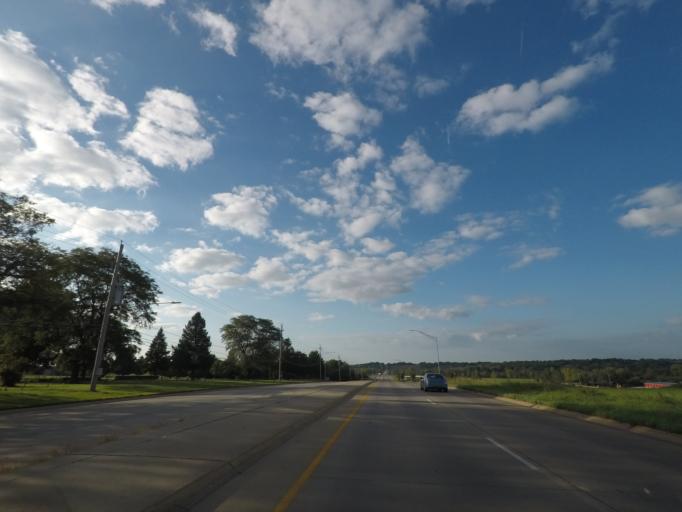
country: US
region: Iowa
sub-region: Warren County
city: Norwalk
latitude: 41.5155
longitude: -93.6451
